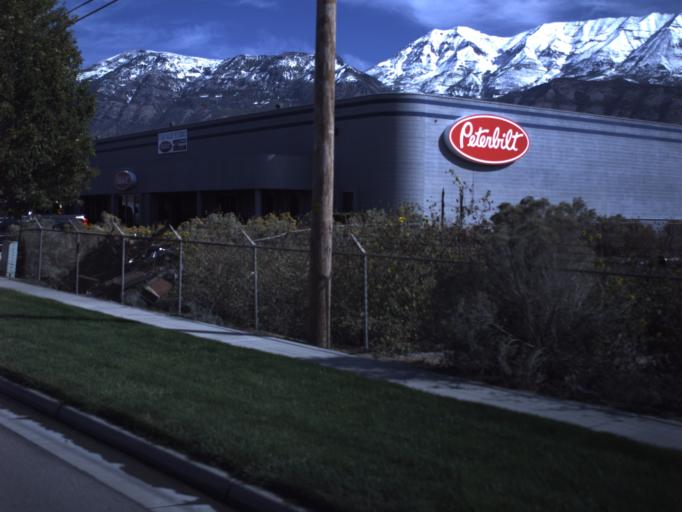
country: US
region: Utah
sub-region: Utah County
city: Lindon
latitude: 40.3432
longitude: -111.7403
